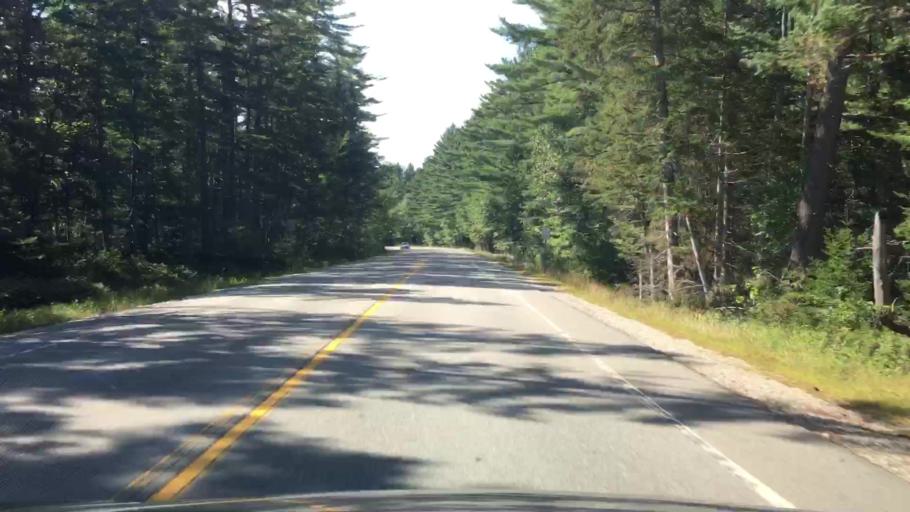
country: US
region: New Hampshire
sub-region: Carroll County
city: Tamworth
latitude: 43.9967
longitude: -71.3531
